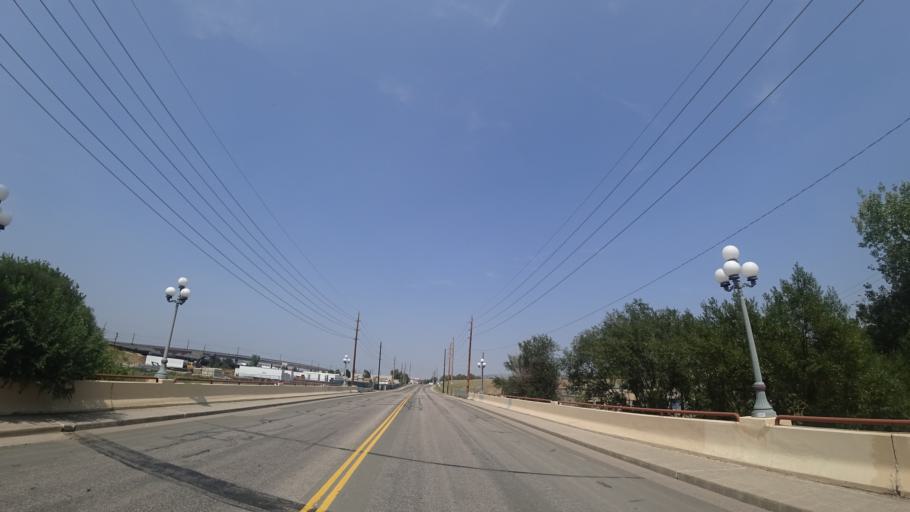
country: US
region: Colorado
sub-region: Arapahoe County
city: Littleton
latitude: 39.6285
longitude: -105.0066
